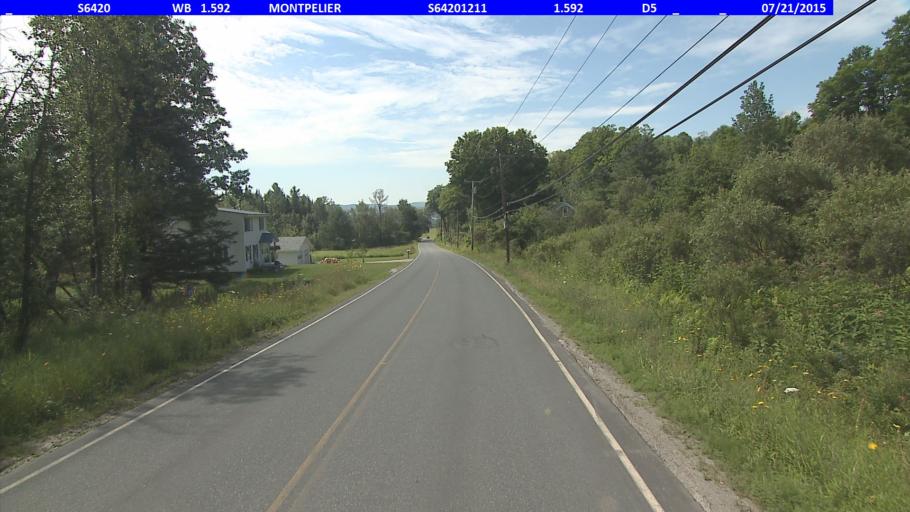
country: US
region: Vermont
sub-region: Washington County
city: Montpelier
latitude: 44.2719
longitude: -72.5572
